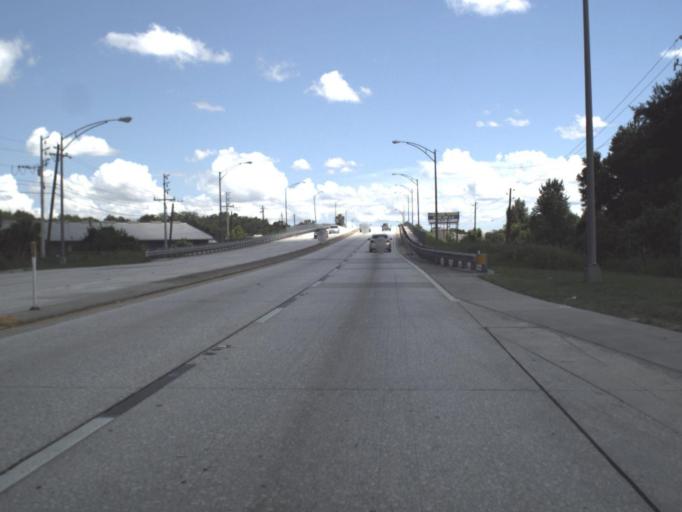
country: US
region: Florida
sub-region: Polk County
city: Lakeland
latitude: 28.0548
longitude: -81.9741
